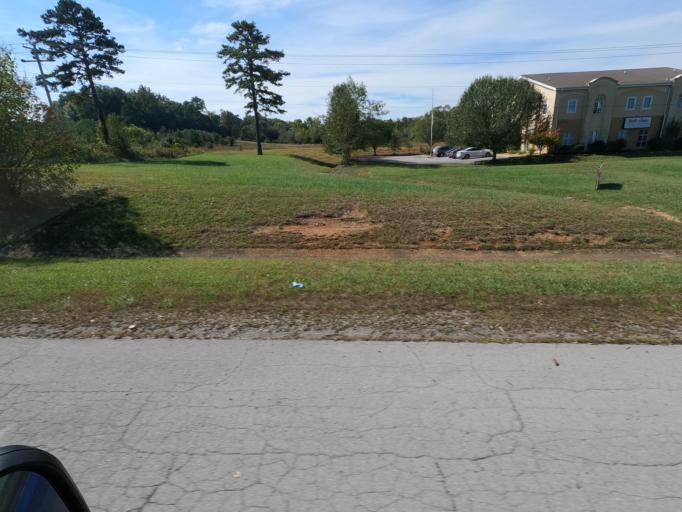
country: US
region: Tennessee
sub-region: Hamblen County
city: Morristown
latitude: 36.2484
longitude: -83.2717
